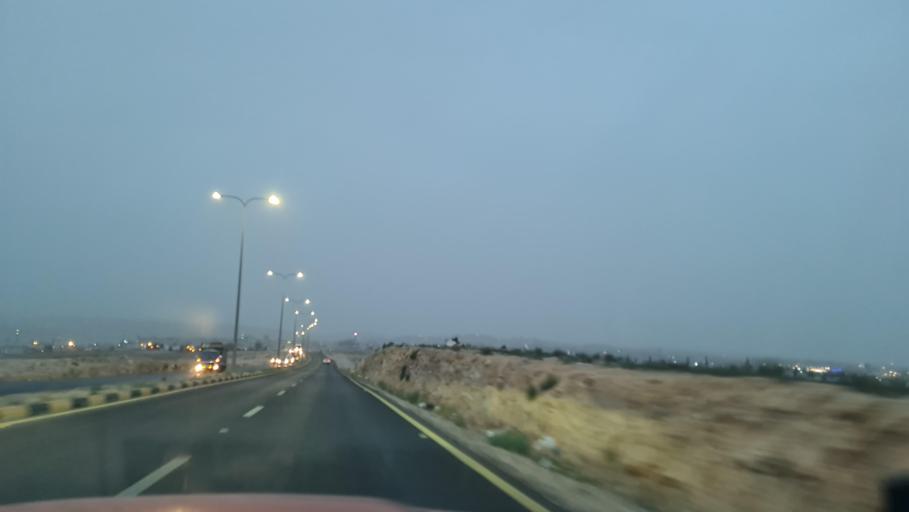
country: JO
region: Zarqa
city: Zarqa
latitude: 32.0503
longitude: 36.1030
